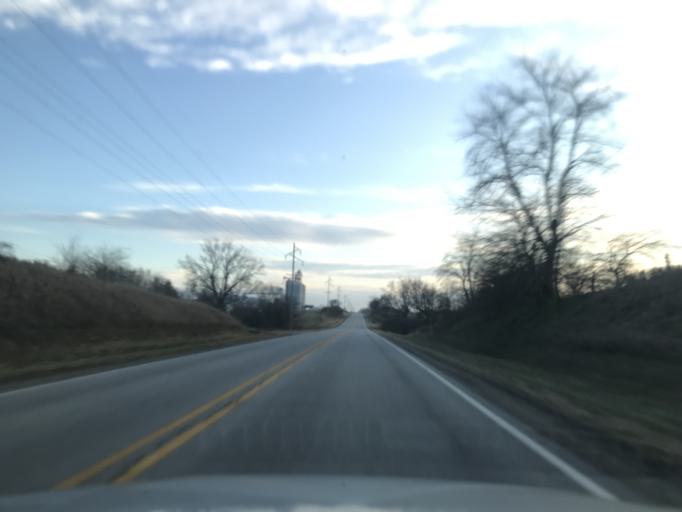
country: US
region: Illinois
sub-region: Mercer County
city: Aledo
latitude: 41.0398
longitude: -90.7460
